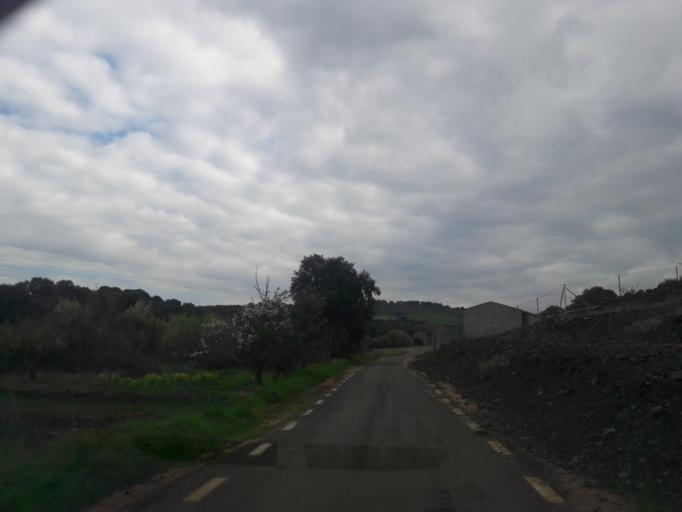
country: ES
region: Castille and Leon
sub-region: Provincia de Salamanca
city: Zamarra
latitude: 40.5039
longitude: -6.4116
